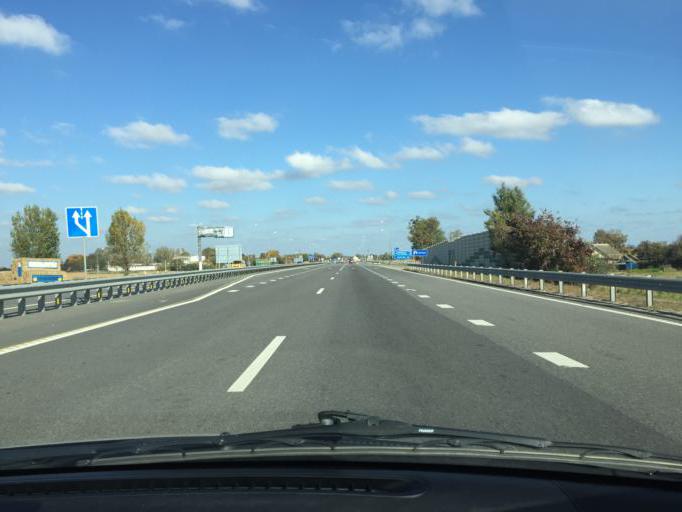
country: BY
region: Minsk
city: Slutsk
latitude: 53.0712
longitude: 27.5562
